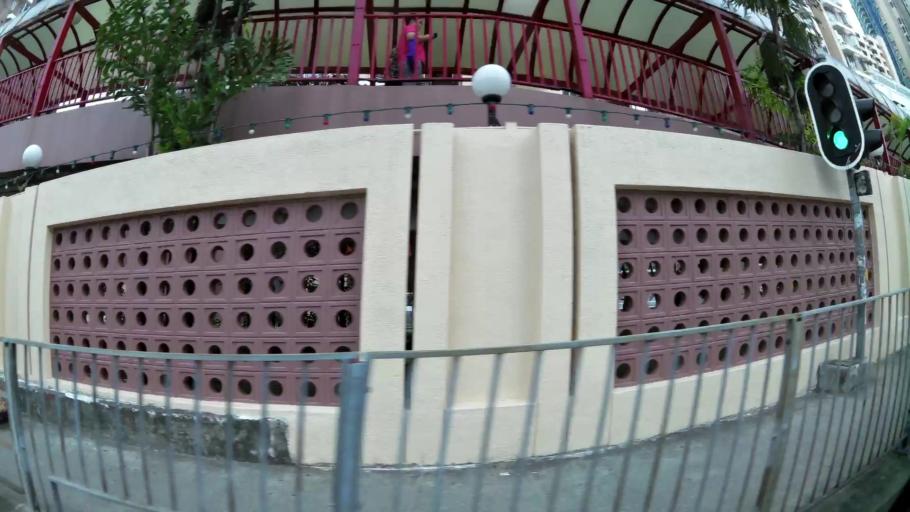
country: HK
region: Sha Tin
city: Sha Tin
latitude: 22.3973
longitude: 114.1998
